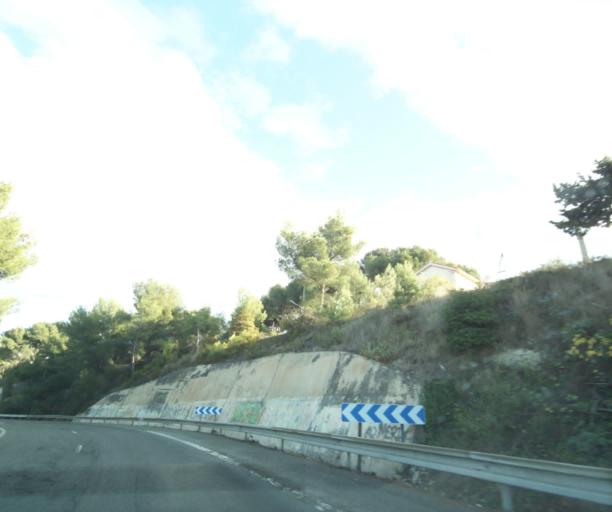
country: FR
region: Provence-Alpes-Cote d'Azur
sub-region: Departement des Bouches-du-Rhone
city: Martigues
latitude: 43.3979
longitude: 5.0791
